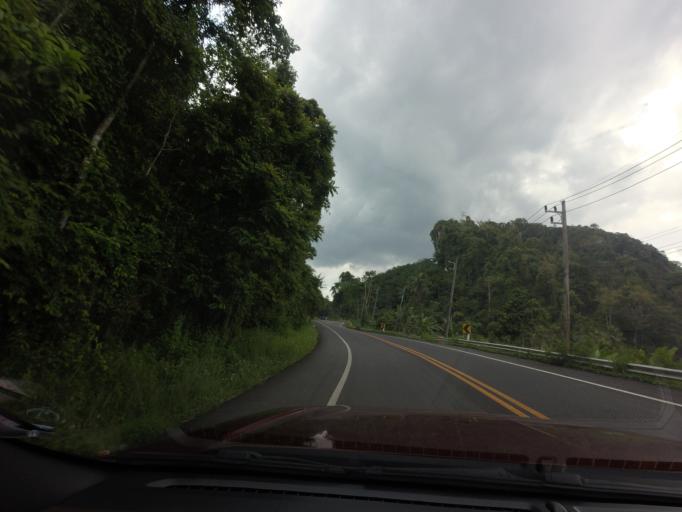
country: TH
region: Yala
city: Than To
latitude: 6.2023
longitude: 101.1711
